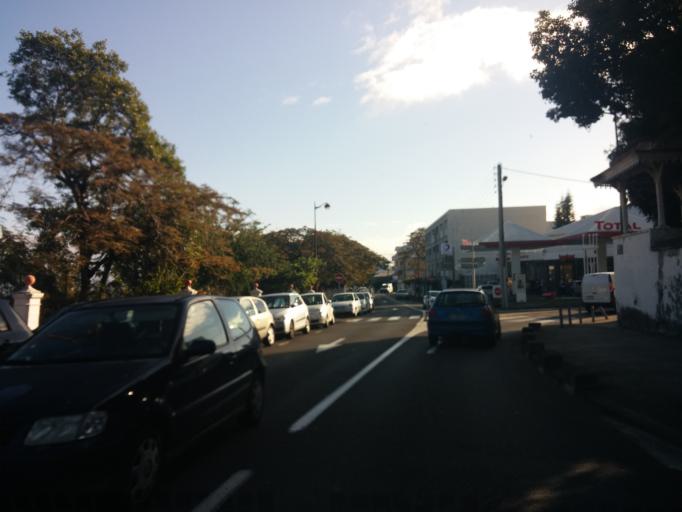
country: RE
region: Reunion
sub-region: Reunion
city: Saint-Denis
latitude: -20.8841
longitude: 55.4474
